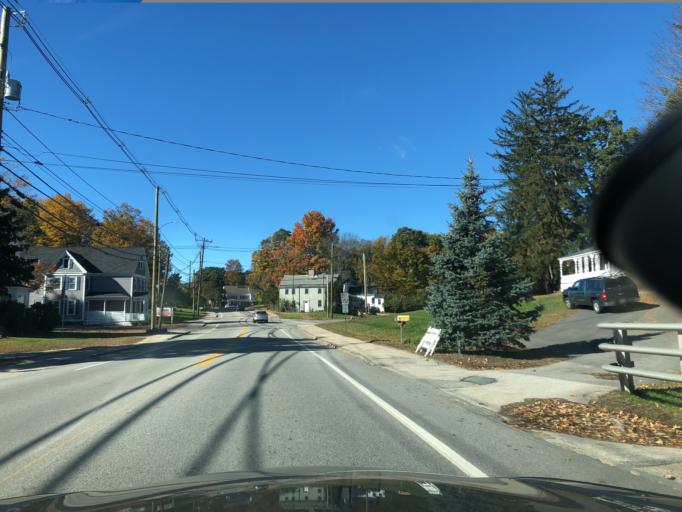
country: US
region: New Hampshire
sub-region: Rockingham County
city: Newmarket
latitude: 43.0768
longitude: -70.9405
